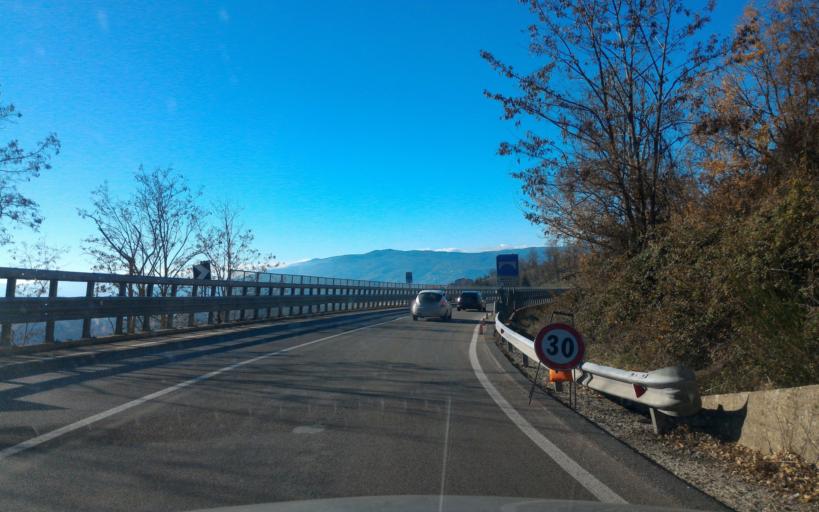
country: IT
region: Calabria
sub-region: Provincia di Cosenza
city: Spezzano Piccolo
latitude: 39.2948
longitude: 16.3543
